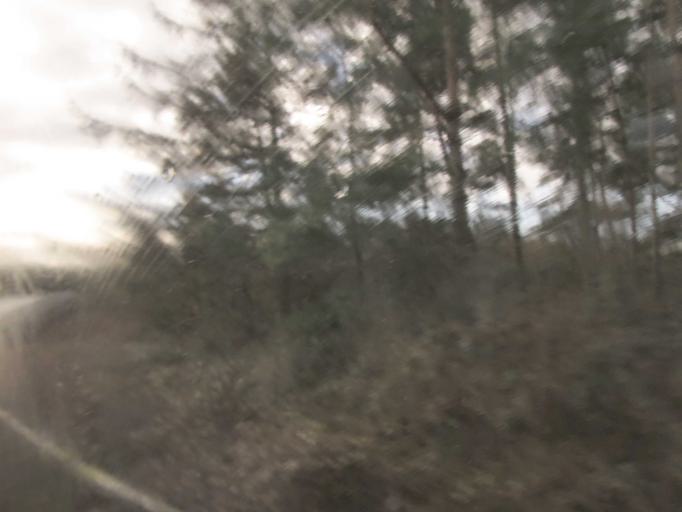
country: GB
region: England
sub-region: Hampshire
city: Basingstoke
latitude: 51.2196
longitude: -1.1582
